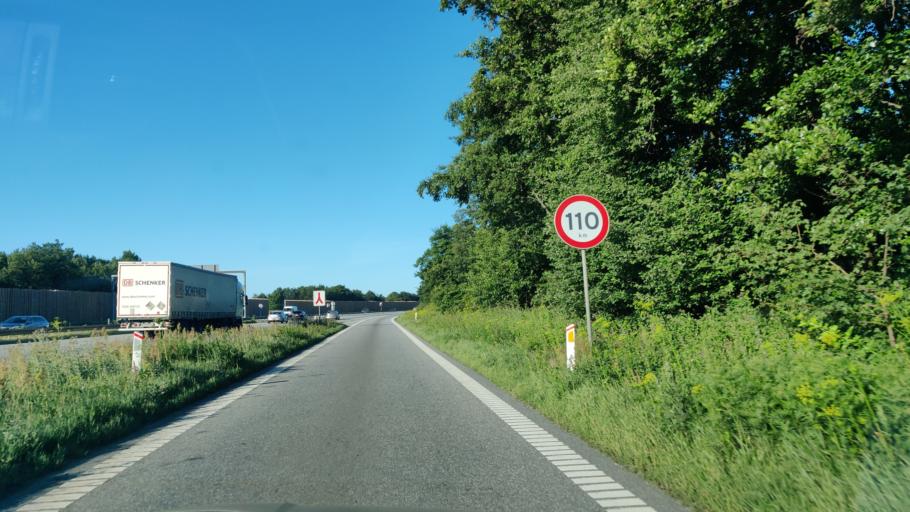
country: DK
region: North Denmark
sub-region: Alborg Kommune
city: Gistrup
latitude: 57.0194
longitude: 9.9593
